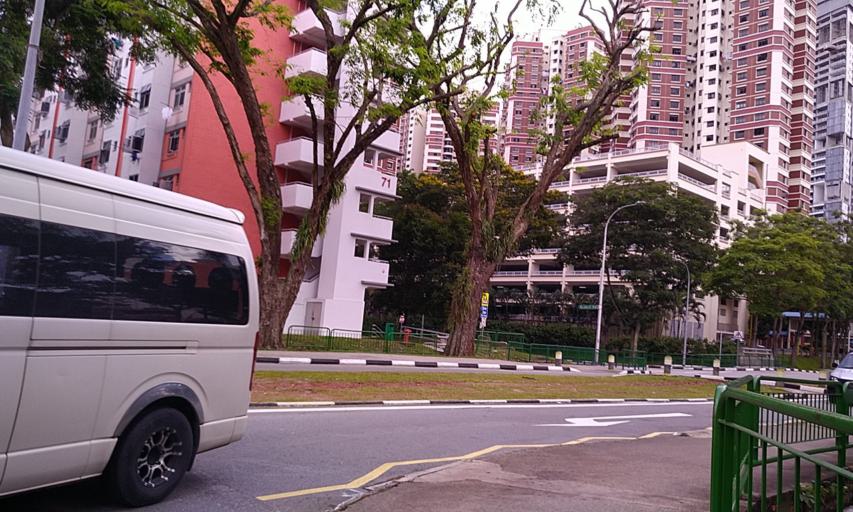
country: SG
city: Singapore
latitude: 1.2871
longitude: 103.8180
